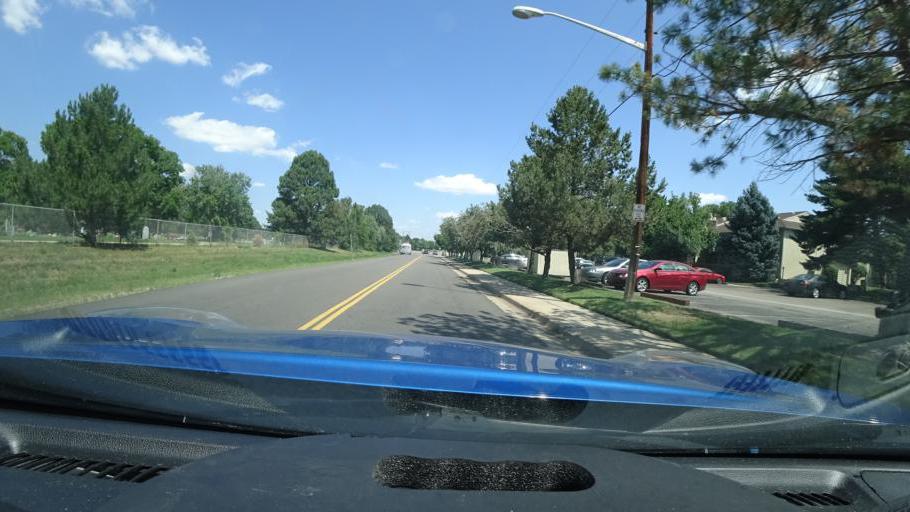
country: US
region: Colorado
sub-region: Arapahoe County
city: Glendale
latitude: 39.7093
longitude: -104.8927
